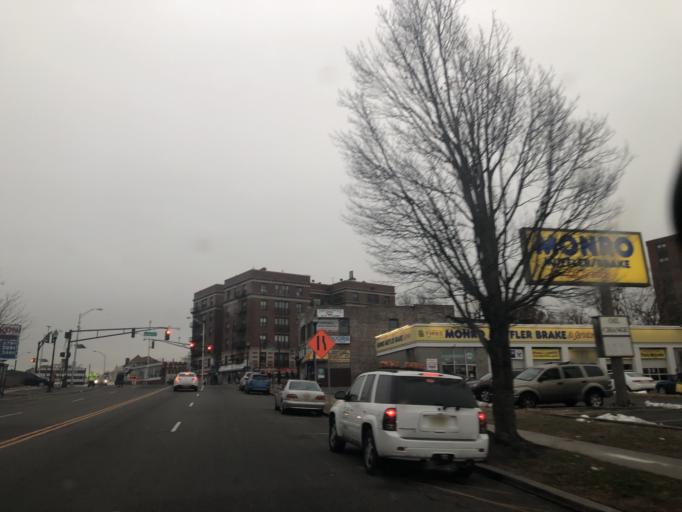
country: US
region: New Jersey
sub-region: Essex County
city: East Orange
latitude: 40.7541
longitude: -74.2140
